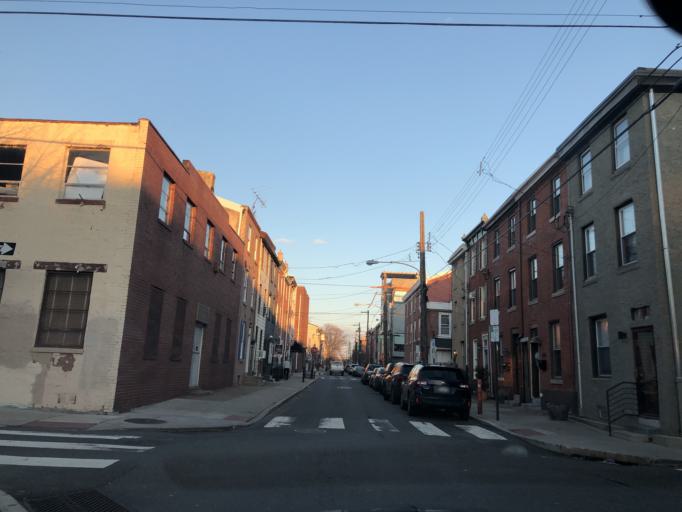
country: US
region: Pennsylvania
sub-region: Philadelphia County
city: Philadelphia
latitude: 39.9729
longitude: -75.1328
